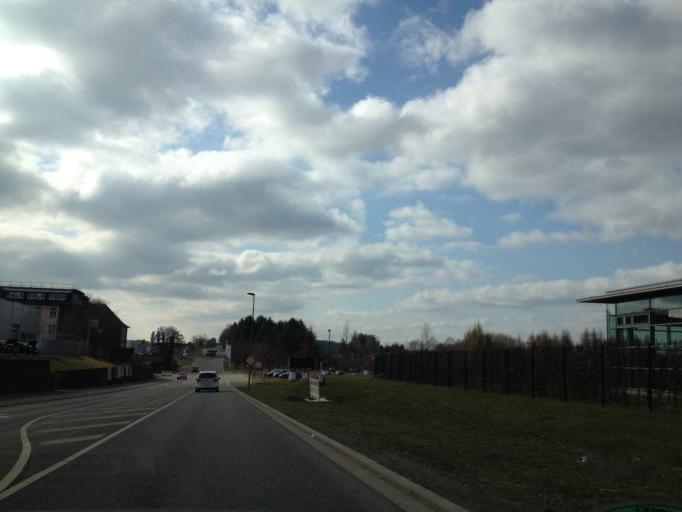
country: DE
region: Saarland
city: Sankt Wendel
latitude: 49.4688
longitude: 7.1441
